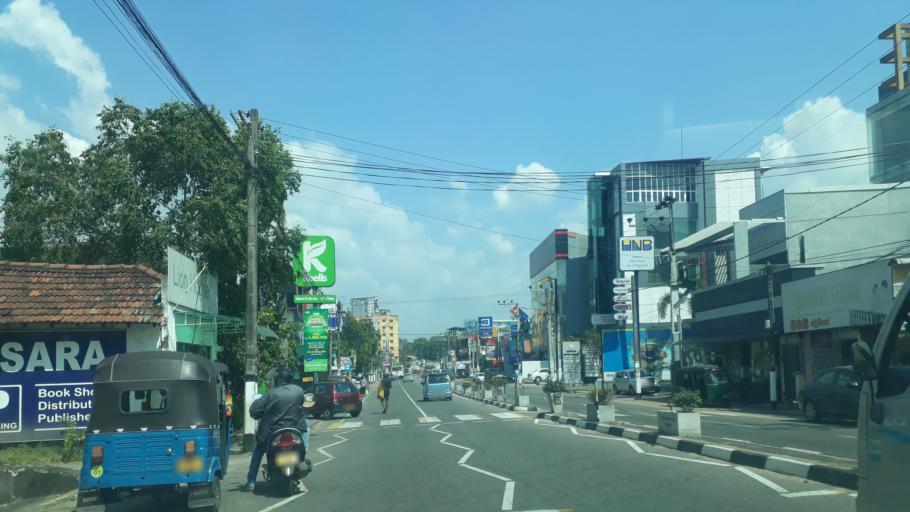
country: LK
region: Western
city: Gampaha
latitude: 7.0912
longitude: 79.9969
